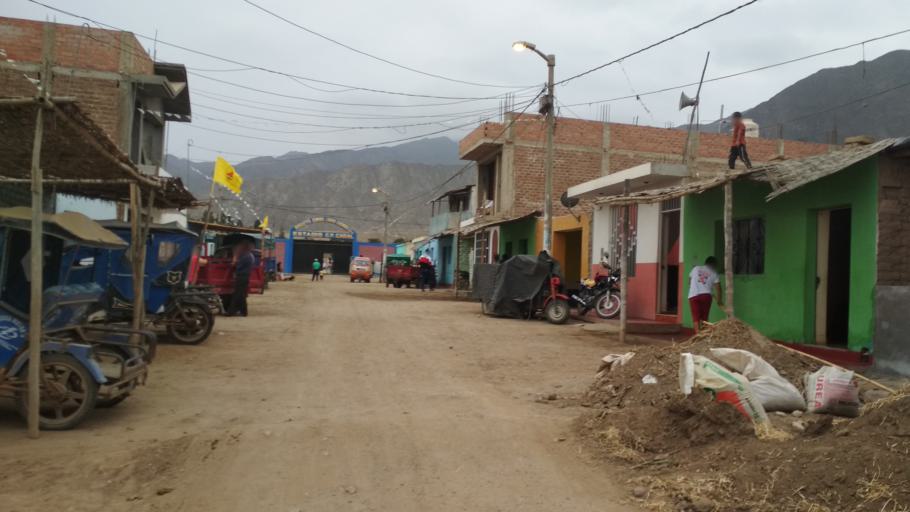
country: PE
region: Lima
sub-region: Huaura
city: Vegueta
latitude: -10.8910
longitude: -77.5010
